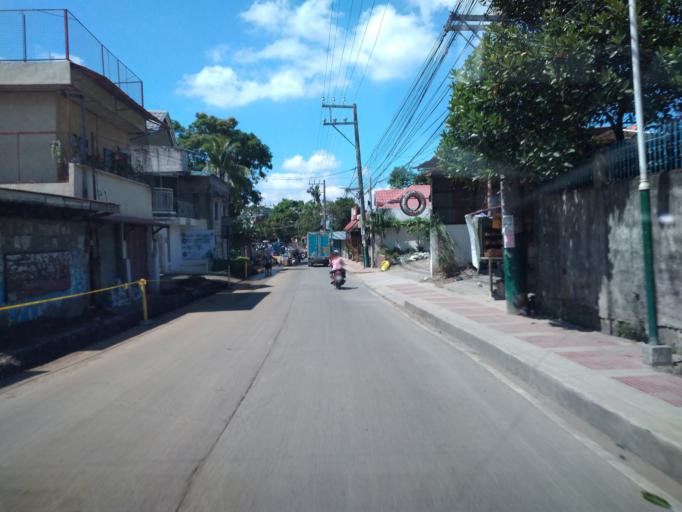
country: PH
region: Central Luzon
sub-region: Province of Bulacan
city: Bitungol
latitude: 14.8598
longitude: 121.0515
